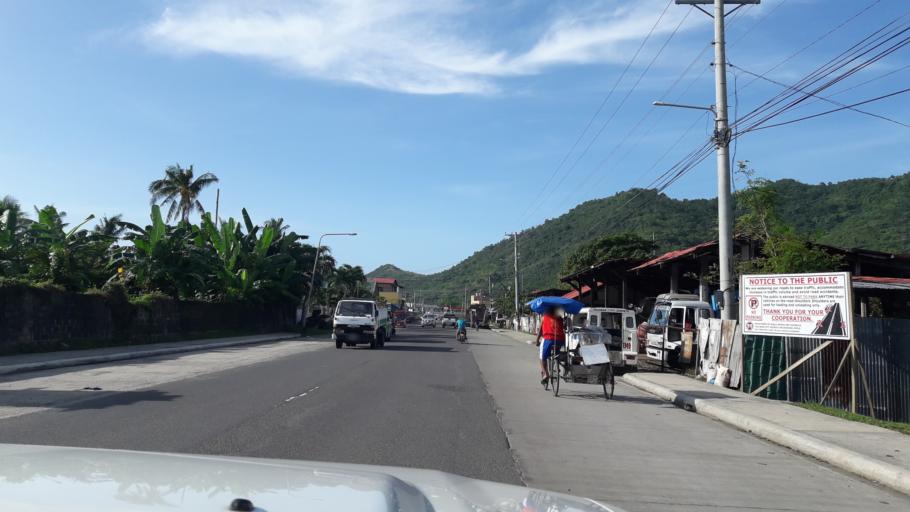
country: PH
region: Eastern Visayas
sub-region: Province of Leyte
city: Pawing
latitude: 11.2096
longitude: 124.9922
